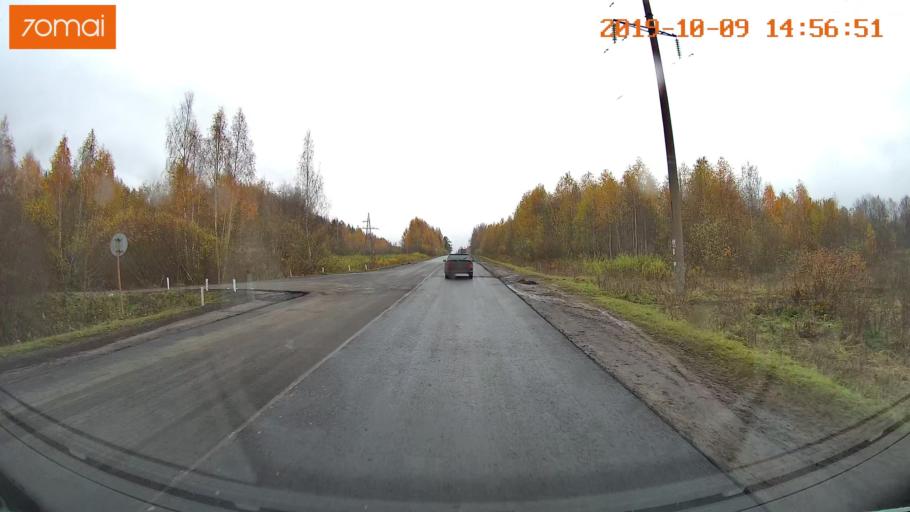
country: RU
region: Kostroma
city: Chistyye Bory
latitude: 58.3427
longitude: 41.6487
